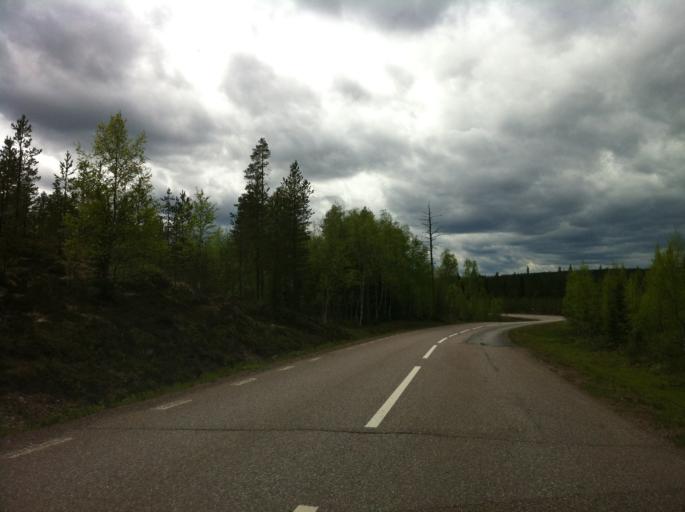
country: NO
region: Hedmark
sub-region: Trysil
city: Innbygda
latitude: 61.5106
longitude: 13.0832
